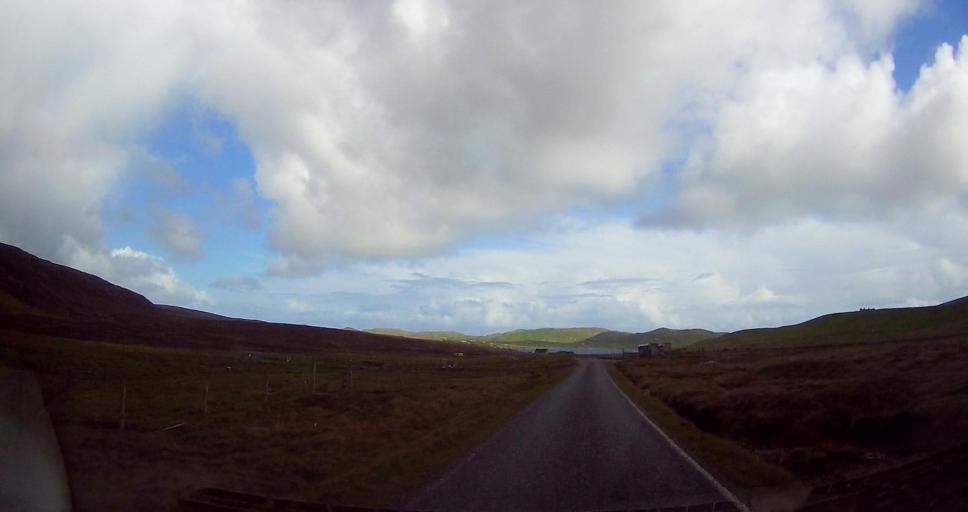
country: GB
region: Scotland
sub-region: Shetland Islands
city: Lerwick
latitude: 60.5666
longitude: -1.3344
